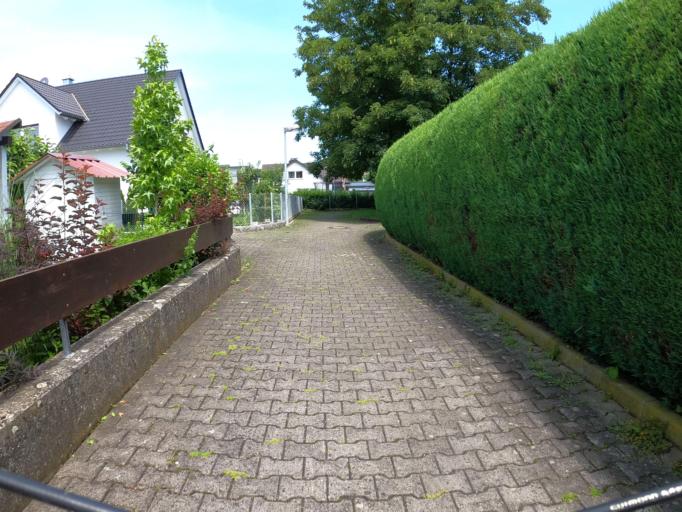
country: DE
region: Bavaria
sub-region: Swabia
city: Leipheim
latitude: 48.4509
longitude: 10.2301
